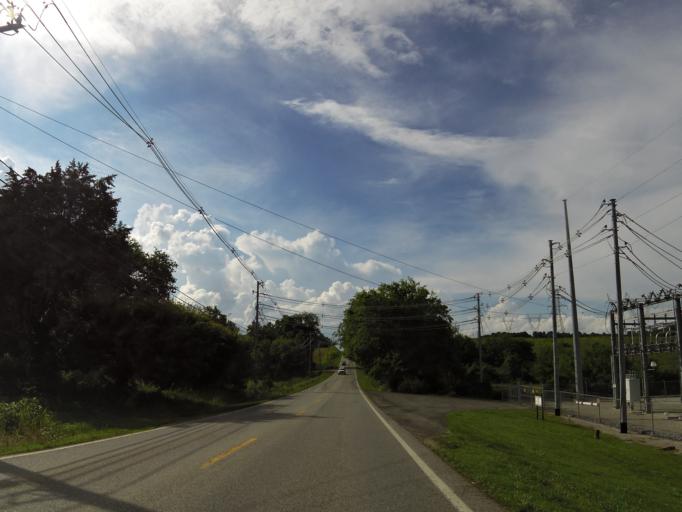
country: US
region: Tennessee
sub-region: Blount County
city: Louisville
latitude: 35.7963
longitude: -84.0158
